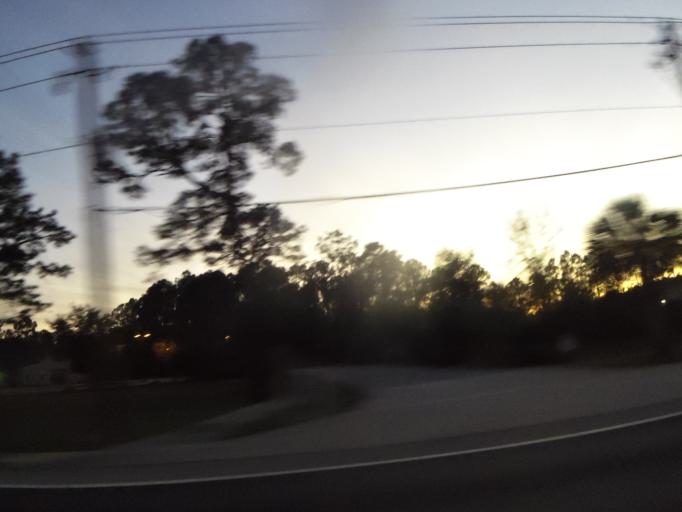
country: US
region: Florida
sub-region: Saint Johns County
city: Saint Augustine South
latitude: 29.8453
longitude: -81.3604
